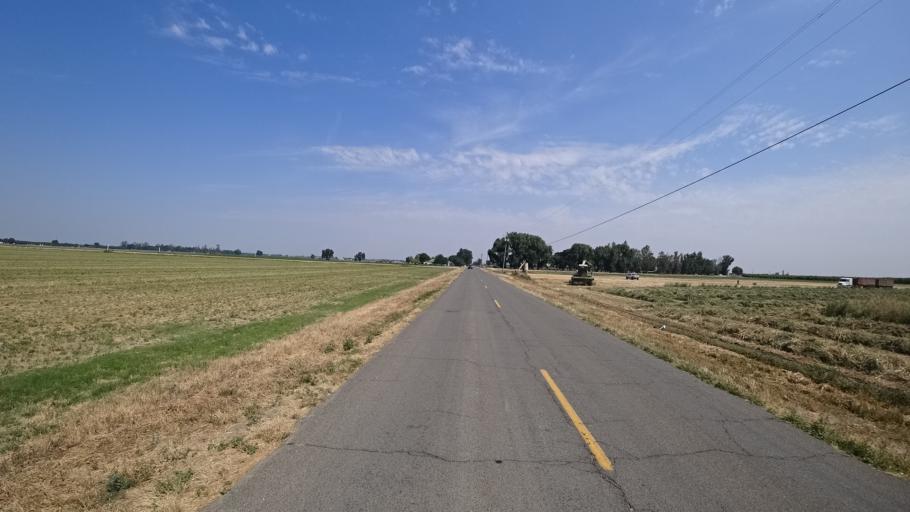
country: US
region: California
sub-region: Kings County
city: Armona
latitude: 36.3601
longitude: -119.7450
